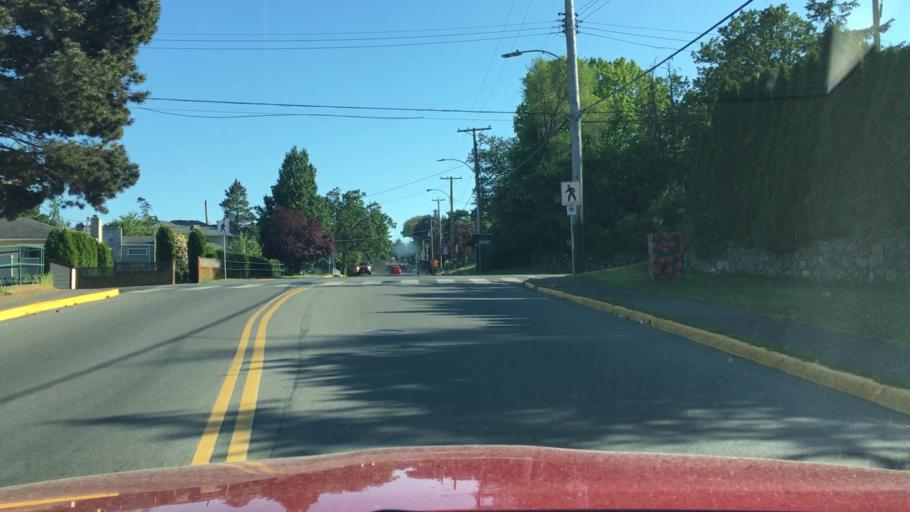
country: CA
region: British Columbia
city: Victoria
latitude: 48.4391
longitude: -123.4018
